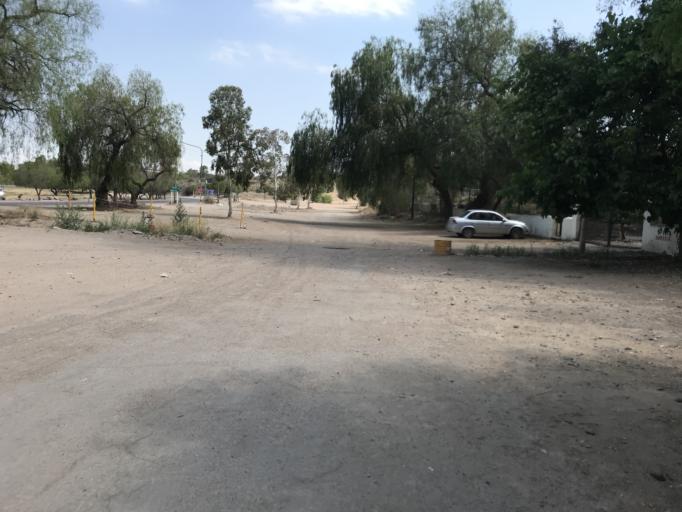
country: AR
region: Mendoza
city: Mendoza
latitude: -32.8892
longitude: -68.8852
